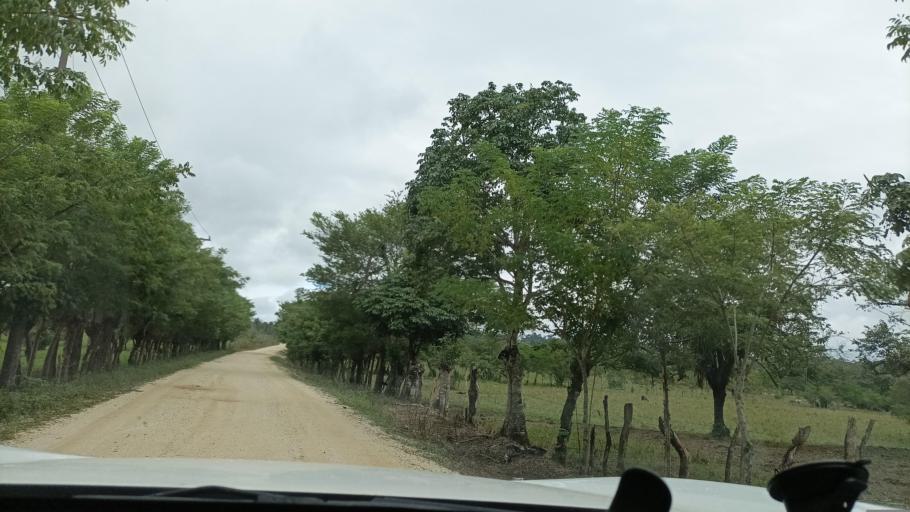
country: MX
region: Veracruz
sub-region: Moloacan
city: Cuichapa
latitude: 17.8225
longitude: -94.3539
